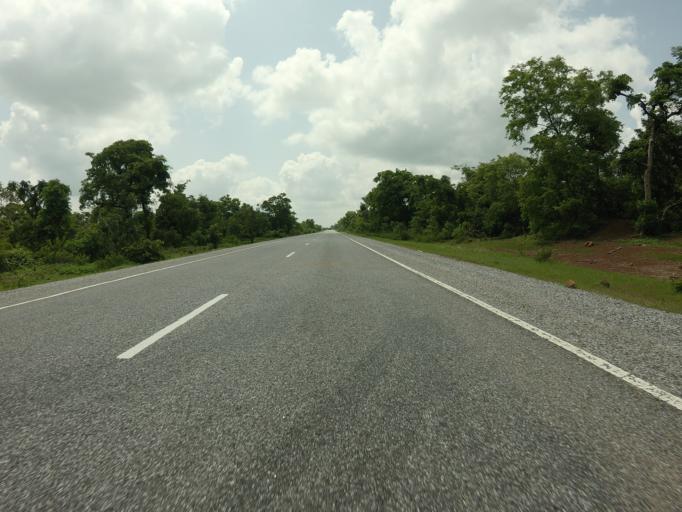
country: GH
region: Northern
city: Tamale
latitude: 9.1224
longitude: -1.6279
